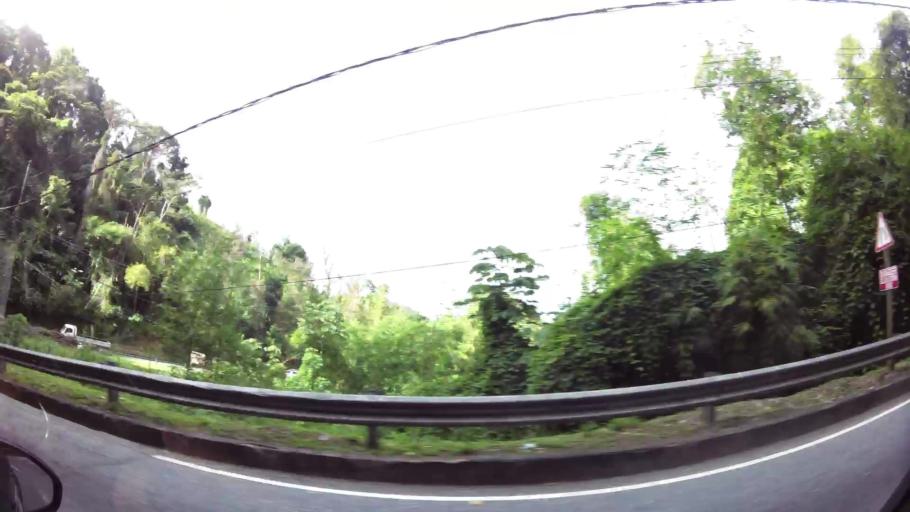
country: TT
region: Diego Martin
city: Petit Valley
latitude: 10.7139
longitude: -61.4984
